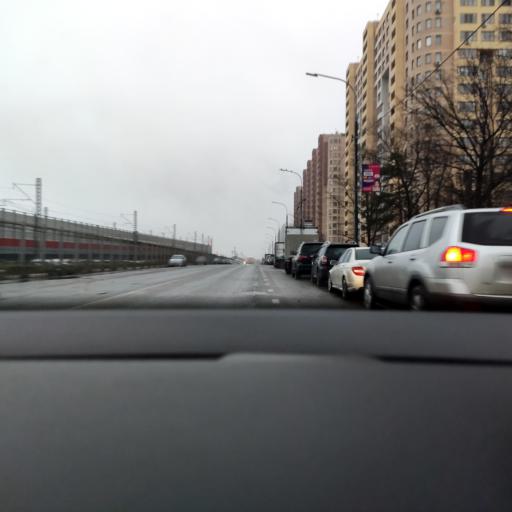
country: RU
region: Moskovskaya
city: Reutov
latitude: 55.7532
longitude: 37.8661
